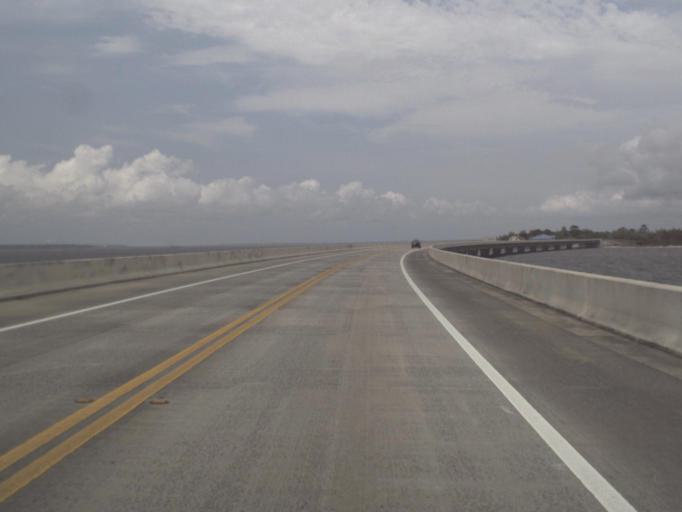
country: US
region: Florida
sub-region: Santa Rosa County
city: Oriole Beach
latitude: 30.4366
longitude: -87.0991
